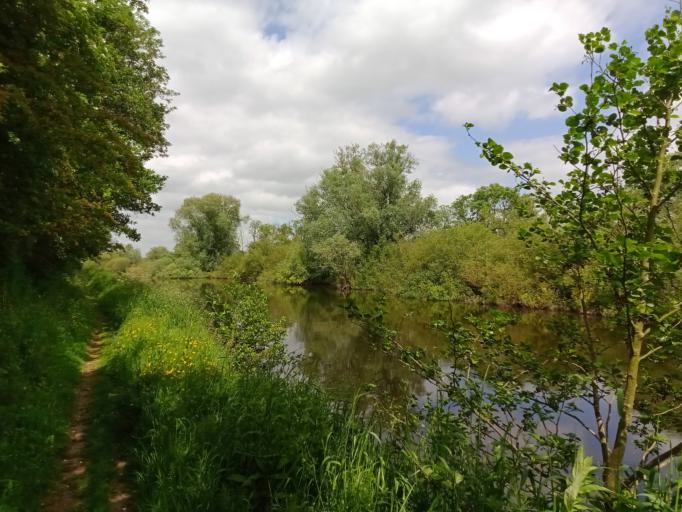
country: IE
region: Leinster
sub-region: County Carlow
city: Carlow
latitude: 52.7987
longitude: -6.9622
